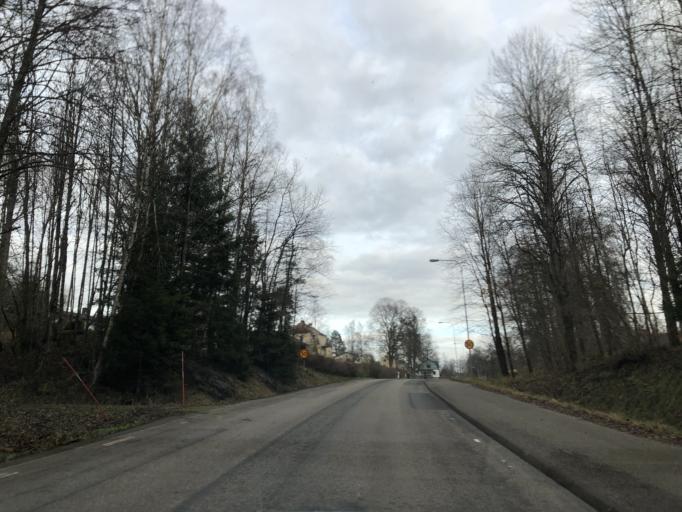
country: SE
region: Vaestra Goetaland
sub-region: Ulricehamns Kommun
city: Ulricehamn
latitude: 57.7255
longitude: 13.3083
